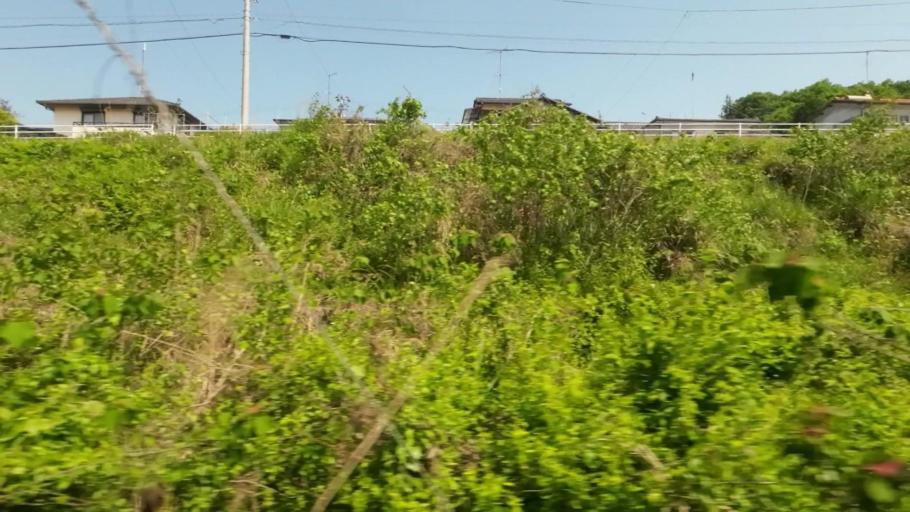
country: JP
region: Ehime
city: Saijo
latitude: 33.9221
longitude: 133.2365
